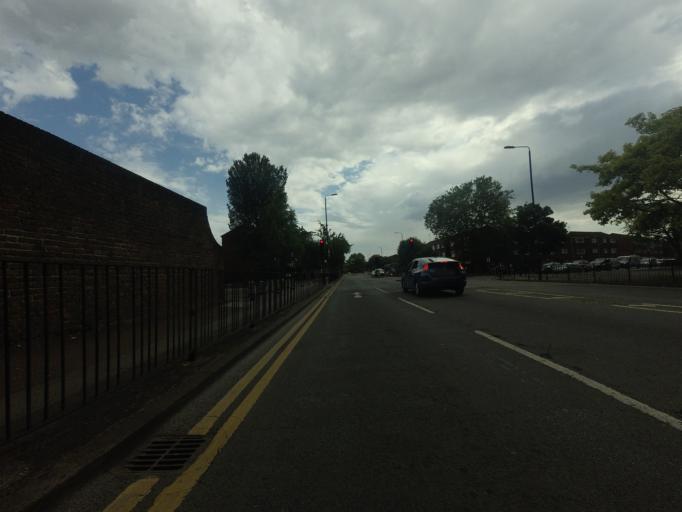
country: GB
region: England
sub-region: Greater London
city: Poplar
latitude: 51.5336
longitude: 0.0083
